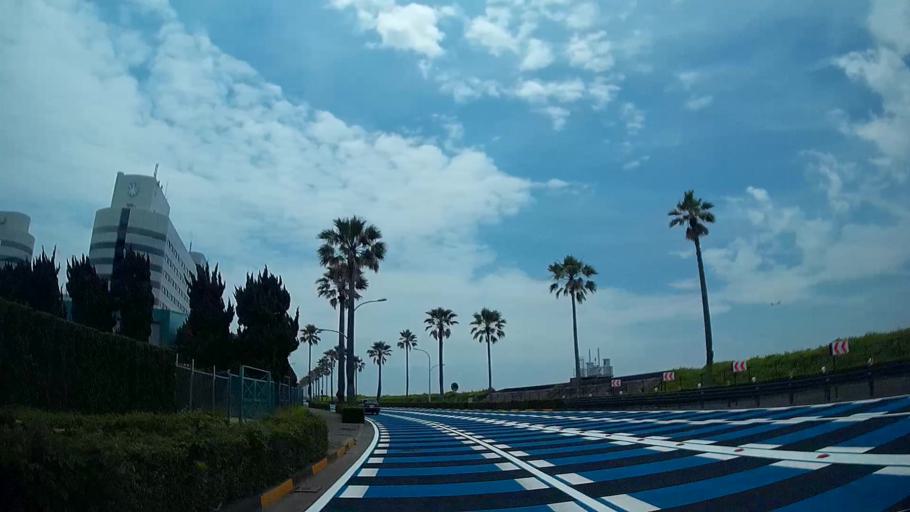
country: JP
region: Tokyo
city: Urayasu
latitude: 35.6332
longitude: 139.8732
